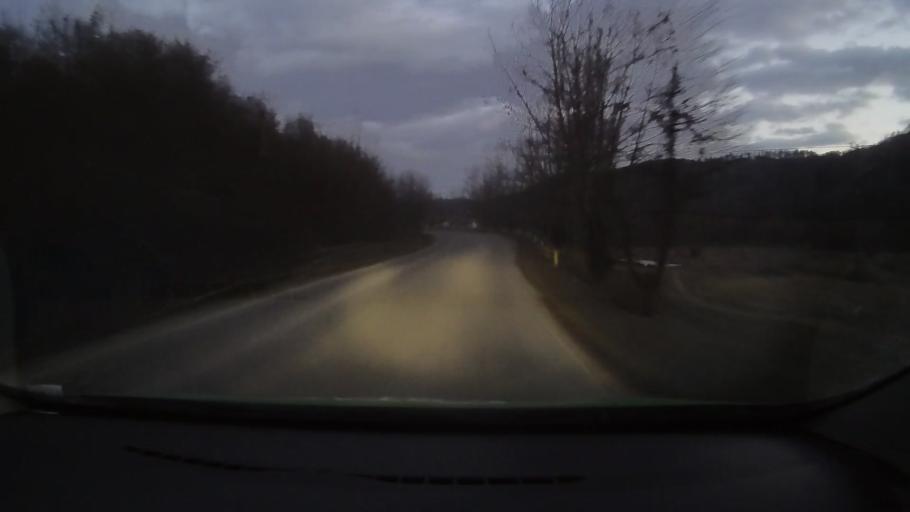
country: RO
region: Prahova
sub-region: Comuna Provita de Jos
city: Provita de Jos
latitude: 45.1242
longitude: 25.6559
